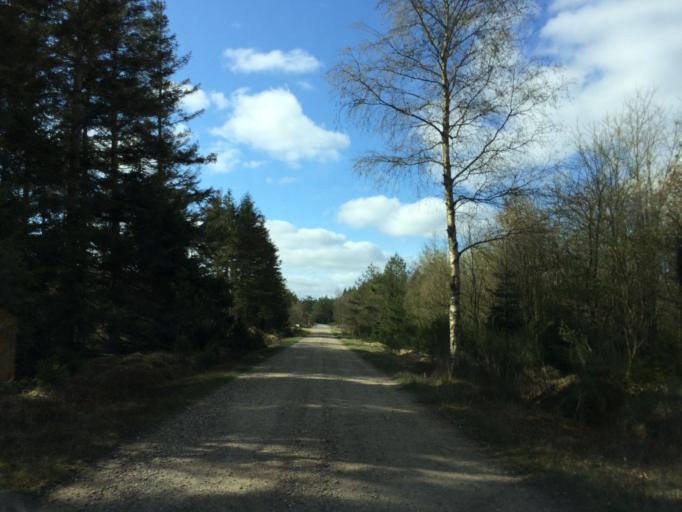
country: DK
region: Central Jutland
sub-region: Holstebro Kommune
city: Ulfborg
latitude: 56.2177
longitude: 8.4588
